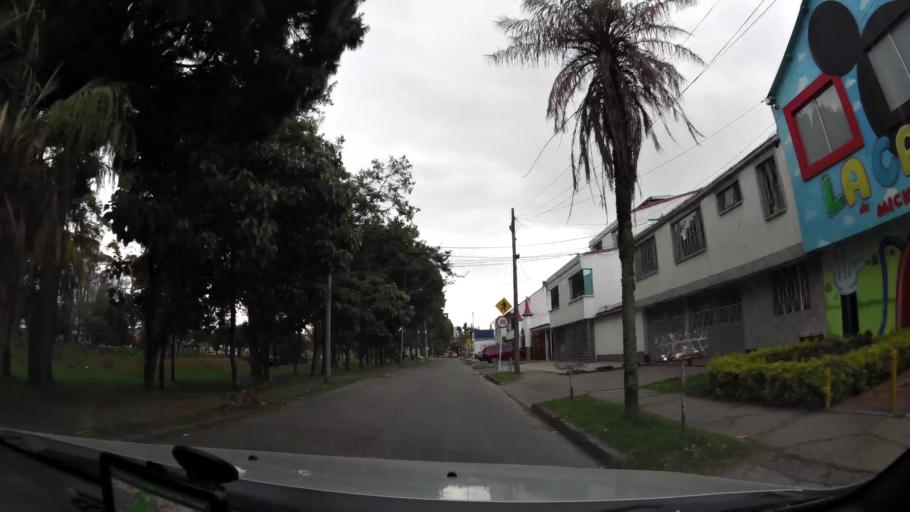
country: CO
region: Bogota D.C.
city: Bogota
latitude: 4.6633
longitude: -74.1187
